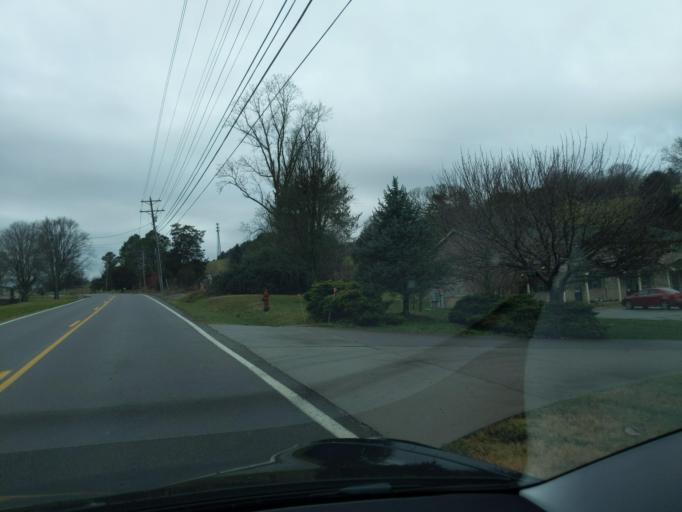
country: US
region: Tennessee
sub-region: Sevier County
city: Sevierville
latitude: 35.9708
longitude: -83.5571
